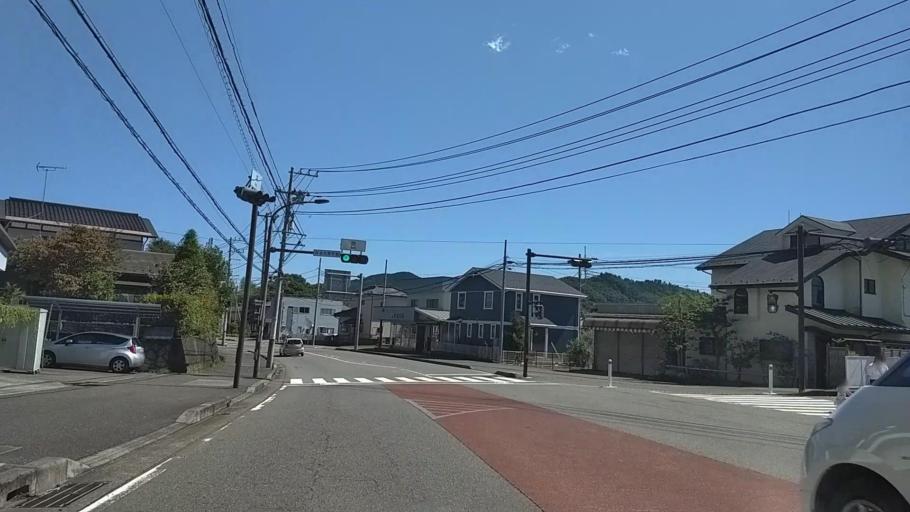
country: JP
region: Tokyo
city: Hachioji
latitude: 35.5662
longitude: 139.2455
